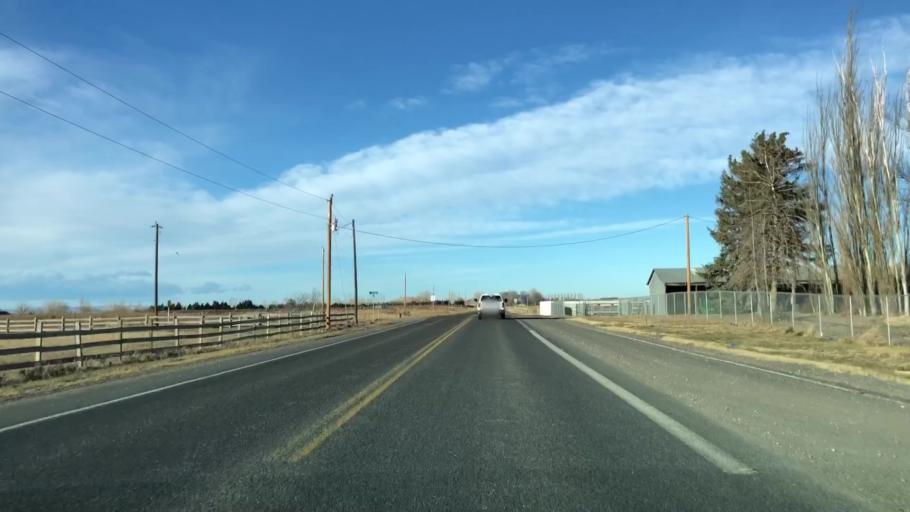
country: US
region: Colorado
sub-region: Weld County
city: Windsor
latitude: 40.4970
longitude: -104.9819
